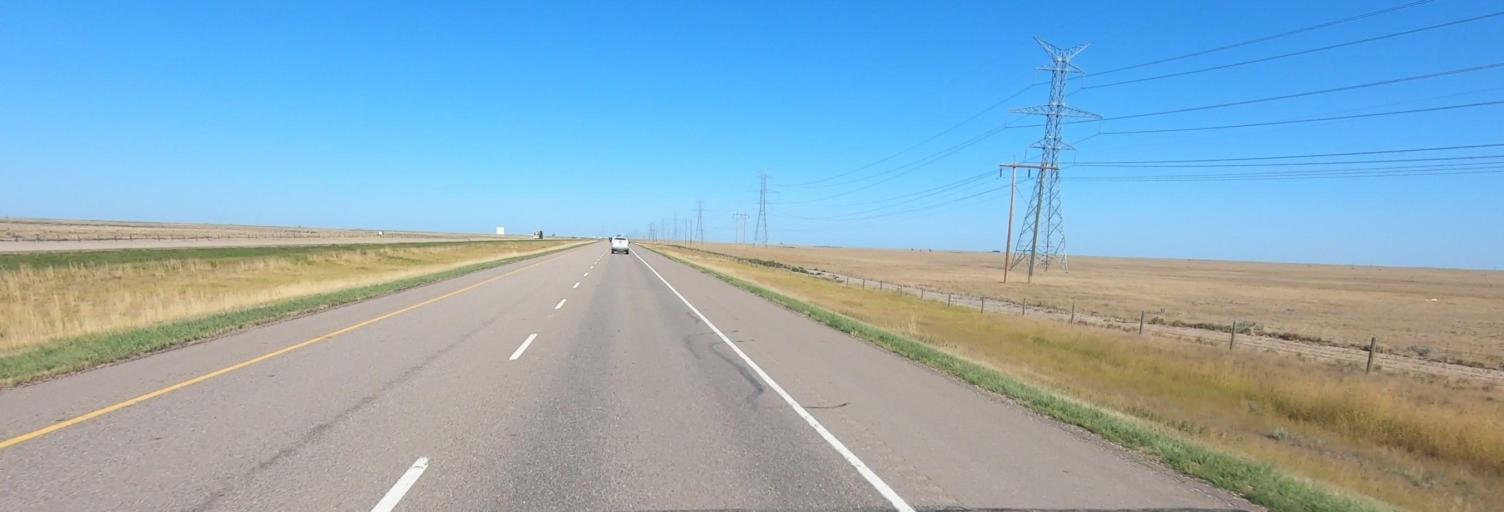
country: CA
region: Alberta
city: Brooks
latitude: 50.4054
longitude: -111.4960
